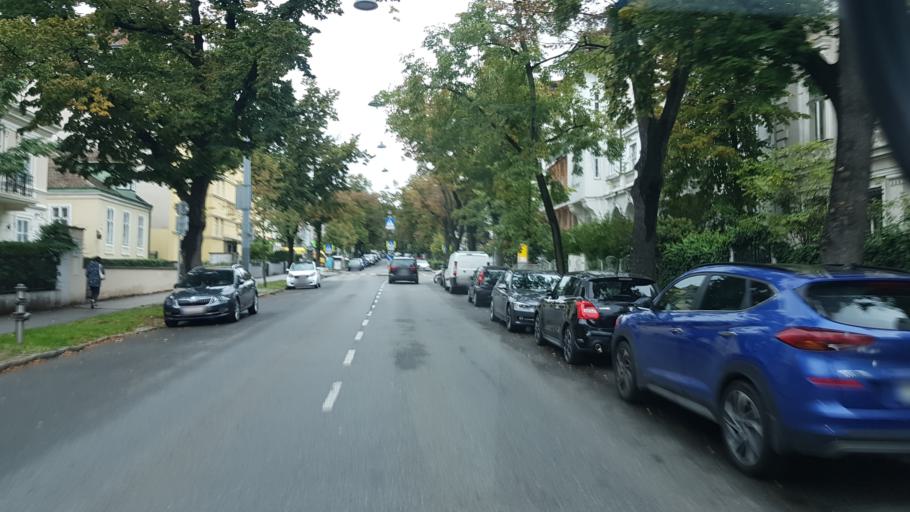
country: AT
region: Vienna
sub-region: Wien Stadt
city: Vienna
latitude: 48.2460
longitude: 16.3400
